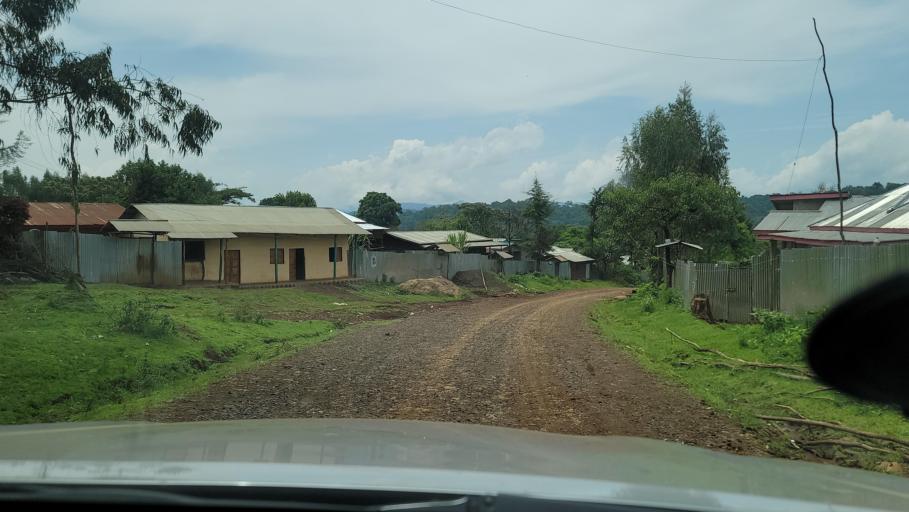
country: ET
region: Oromiya
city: Agaro
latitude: 7.7370
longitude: 36.2582
